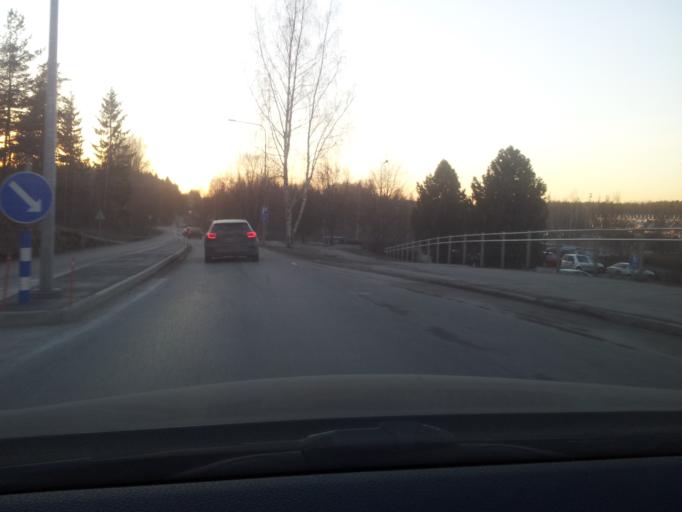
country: FI
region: Uusimaa
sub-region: Helsinki
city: Kilo
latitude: 60.2226
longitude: 24.8034
